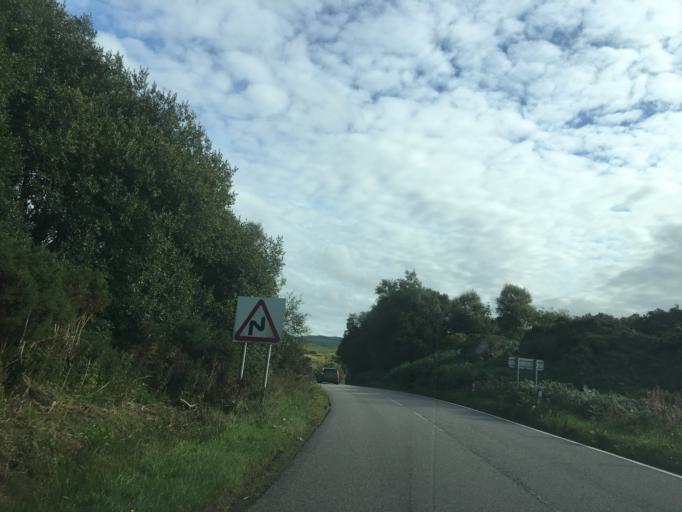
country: GB
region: Scotland
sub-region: Argyll and Bute
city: Oban
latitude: 56.3870
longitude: -5.4586
